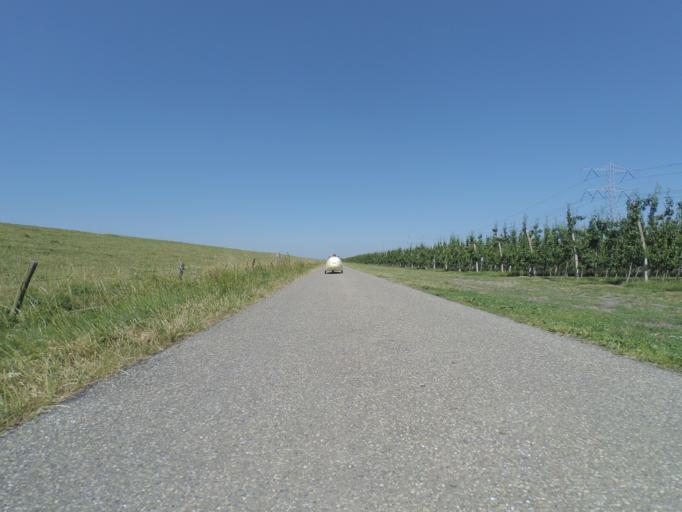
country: NL
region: Zeeland
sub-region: Gemeente Reimerswaal
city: Yerseke
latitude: 51.4384
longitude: 4.1086
